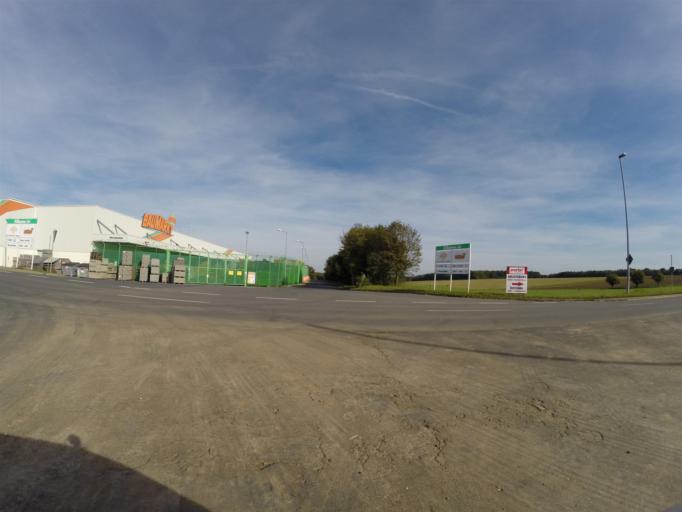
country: DE
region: Thuringia
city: Grossschwabhausen
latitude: 50.9565
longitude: 11.5079
